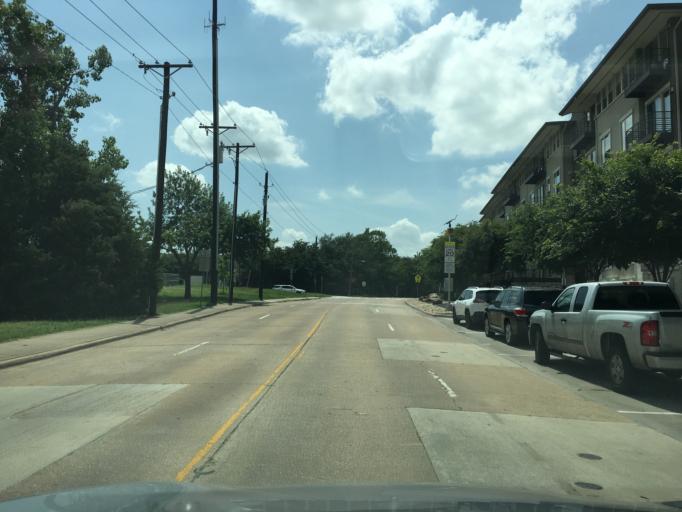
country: US
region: Texas
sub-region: Dallas County
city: Addison
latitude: 32.9488
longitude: -96.8183
